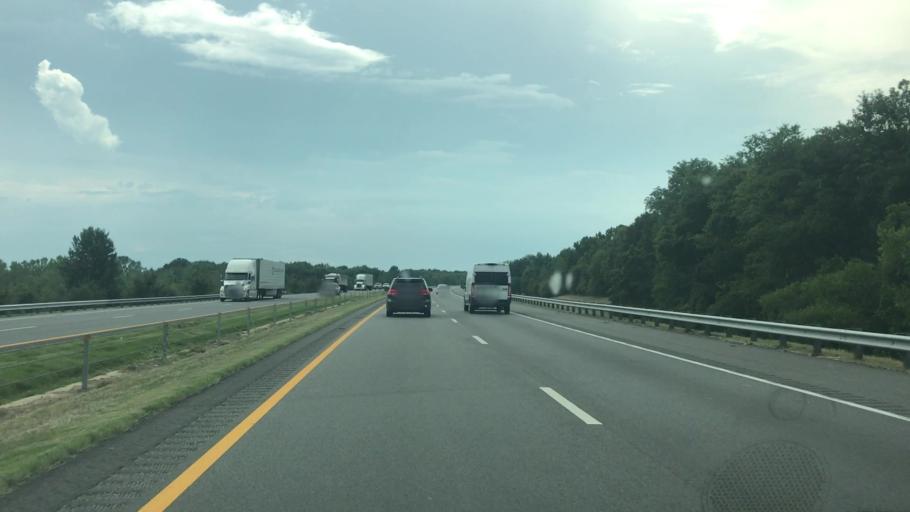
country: US
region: Arkansas
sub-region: Monroe County
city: Brinkley
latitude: 34.8769
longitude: -91.2708
